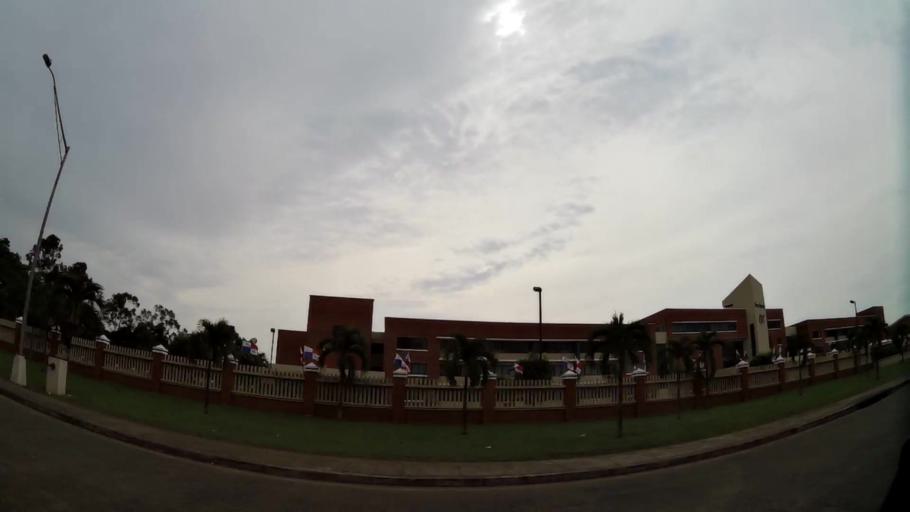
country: PA
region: Panama
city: San Miguelito
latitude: 9.0204
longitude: -79.4597
